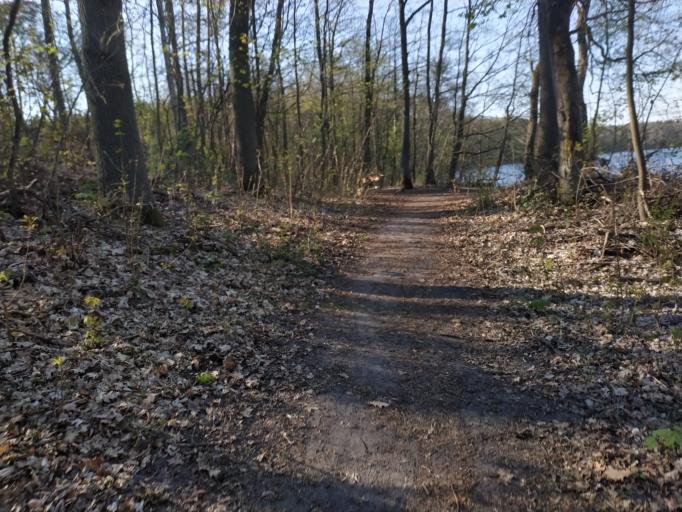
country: DE
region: Brandenburg
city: Petershagen
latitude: 52.5661
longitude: 13.8271
